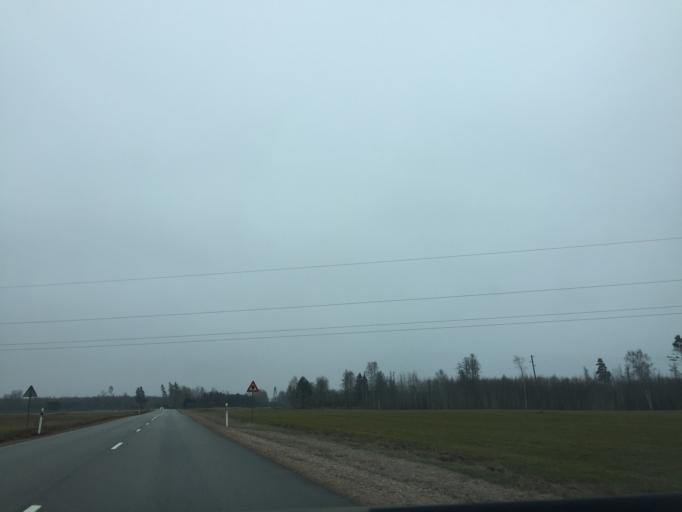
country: LV
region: Lecava
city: Iecava
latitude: 56.6076
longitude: 24.0684
